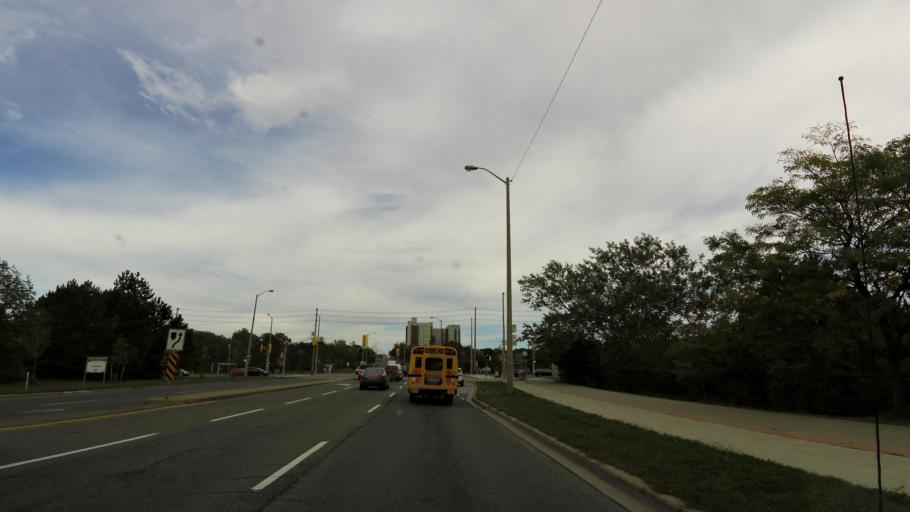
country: CA
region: Ontario
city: Etobicoke
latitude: 43.6841
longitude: -79.4999
